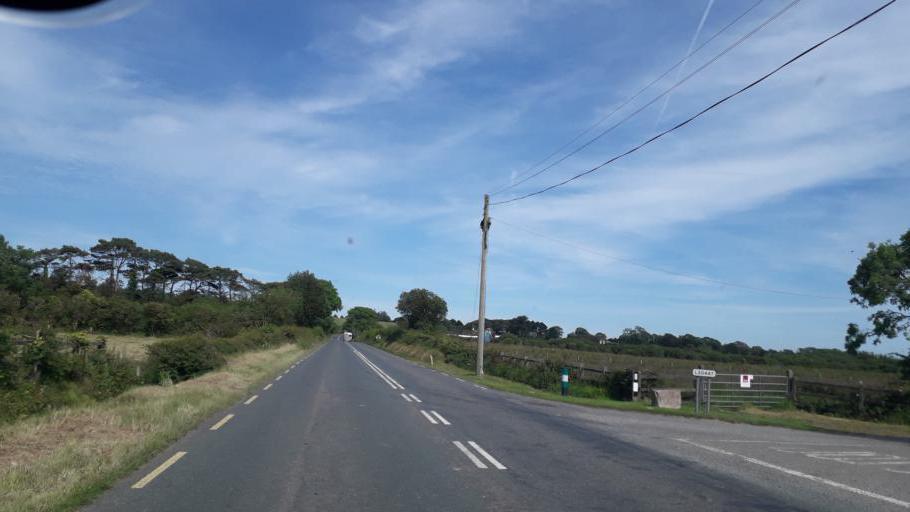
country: IE
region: Leinster
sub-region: Loch Garman
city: Loch Garman
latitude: 52.2892
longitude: -6.6068
